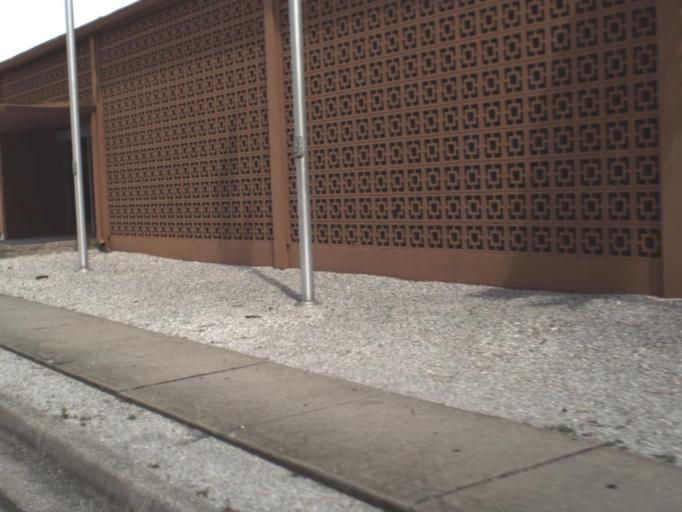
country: US
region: Florida
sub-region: Sarasota County
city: North Sarasota
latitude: 27.3724
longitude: -82.5534
